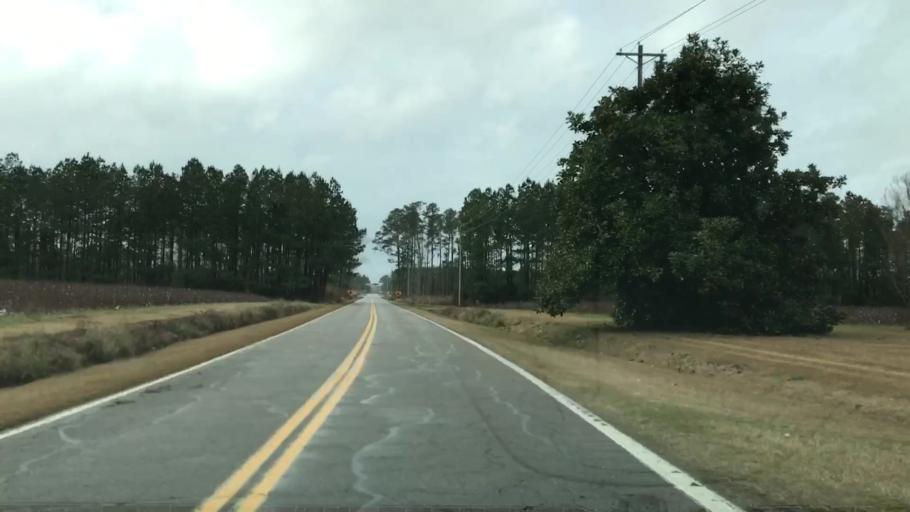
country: US
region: South Carolina
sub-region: Florence County
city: Johnsonville
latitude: 33.6691
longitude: -79.3134
